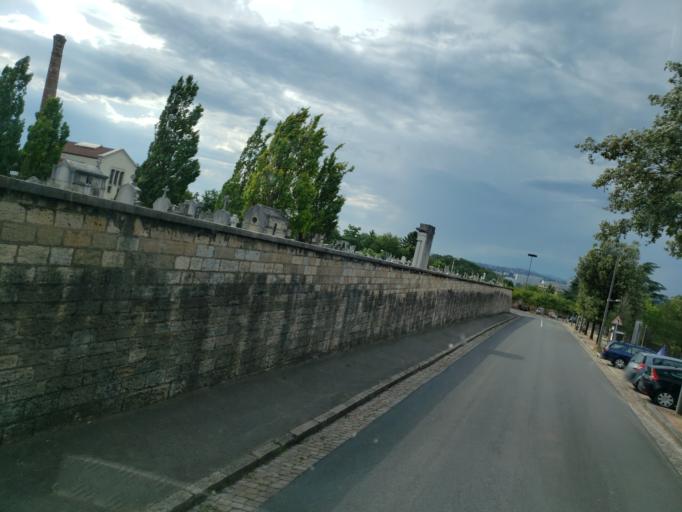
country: FR
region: Rhone-Alpes
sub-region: Departement du Rhone
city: Tassin-la-Demi-Lune
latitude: 45.7618
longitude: 4.8144
